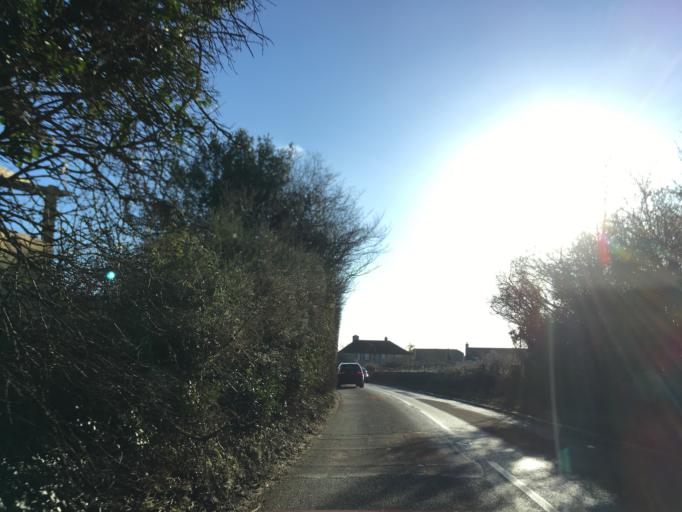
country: GB
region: England
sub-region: Wiltshire
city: Biddestone
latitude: 51.4887
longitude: -2.1950
